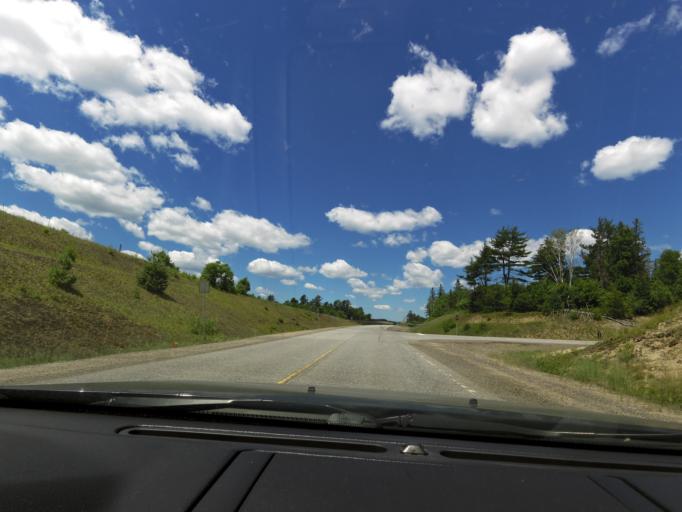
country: CA
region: Ontario
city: Huntsville
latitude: 45.5140
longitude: -79.3068
